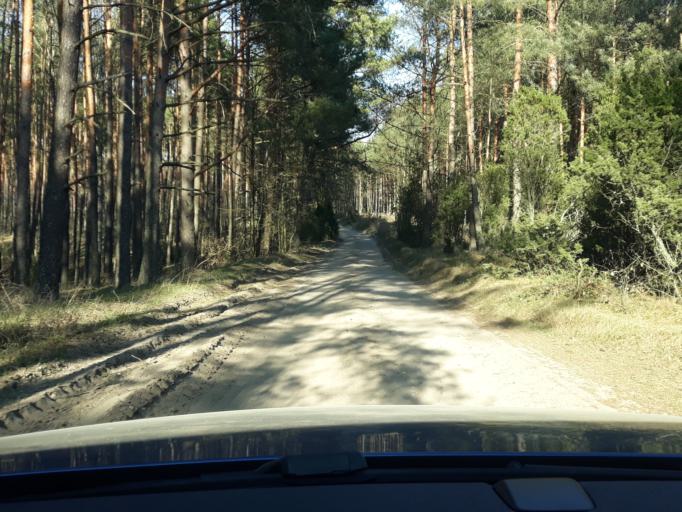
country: PL
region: Pomeranian Voivodeship
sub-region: Powiat bytowski
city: Lipnica
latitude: 53.9099
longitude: 17.4290
